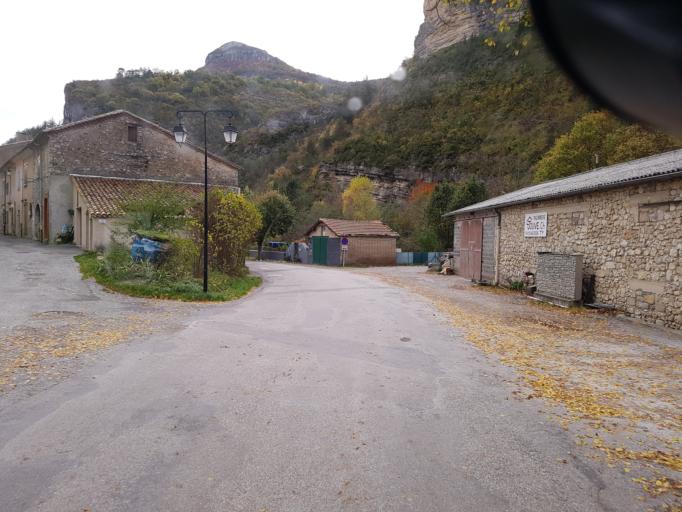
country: FR
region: Provence-Alpes-Cote d'Azur
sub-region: Departement des Hautes-Alpes
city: Serres
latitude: 44.3135
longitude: 5.6891
